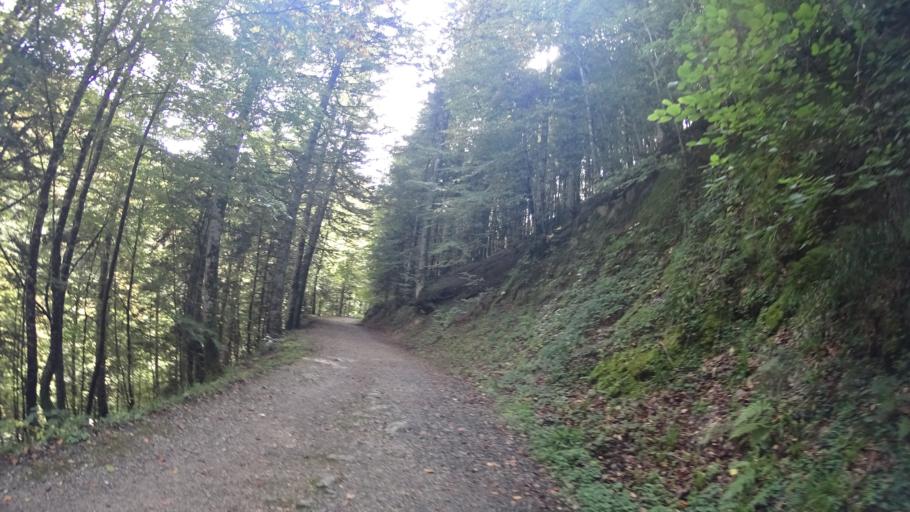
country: ES
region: Navarre
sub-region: Provincia de Navarra
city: Oronz
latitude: 42.9941
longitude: -1.1035
